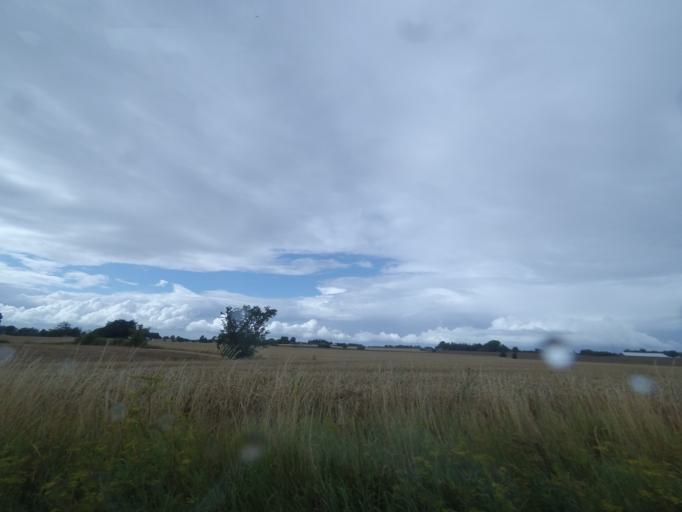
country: DK
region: South Denmark
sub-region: Nordfyns Kommune
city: Sonderso
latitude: 55.4787
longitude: 10.2281
